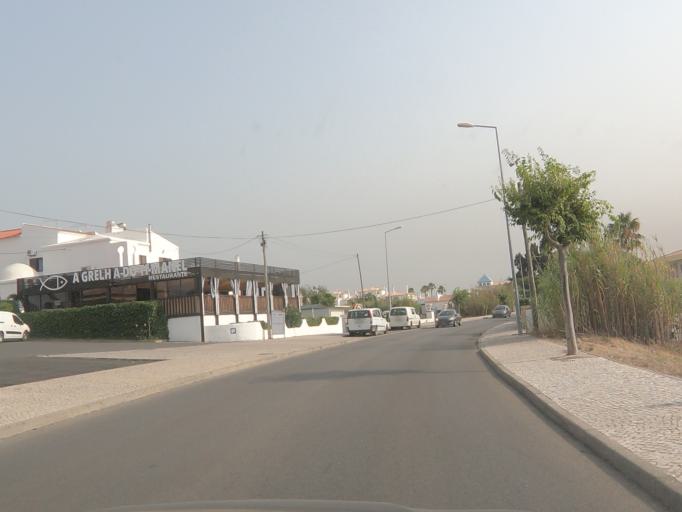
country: PT
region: Faro
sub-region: Albufeira
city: Guia
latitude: 37.0861
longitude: -8.3095
